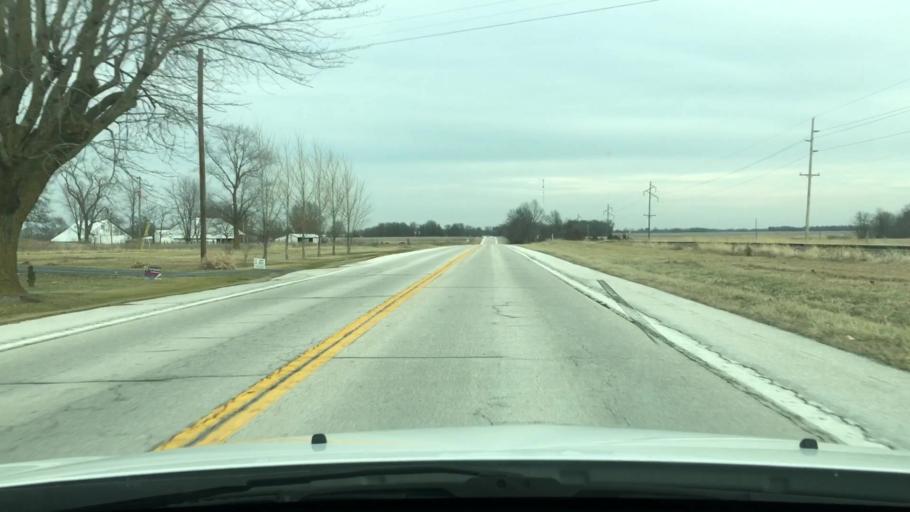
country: US
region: Missouri
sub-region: Audrain County
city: Vandalia
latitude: 39.3324
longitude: -91.4339
